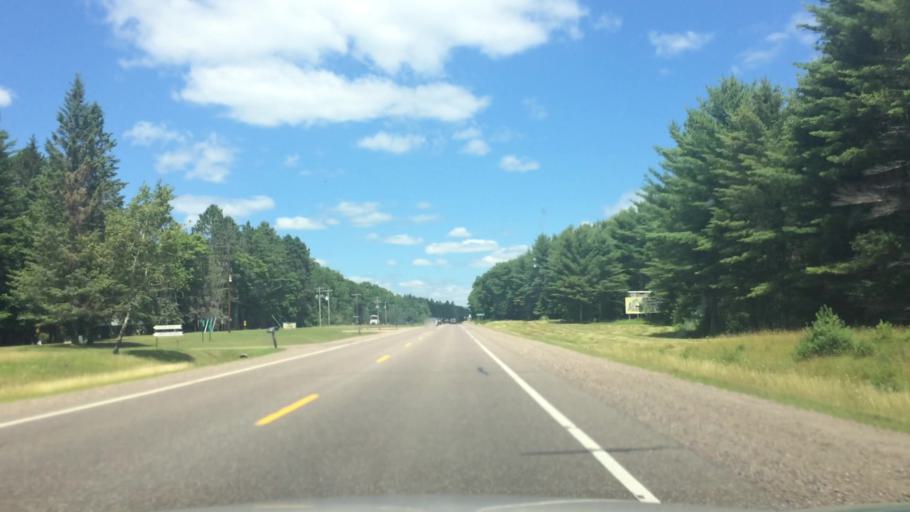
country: US
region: Wisconsin
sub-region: Vilas County
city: Lac du Flambeau
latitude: 45.9762
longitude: -89.6992
